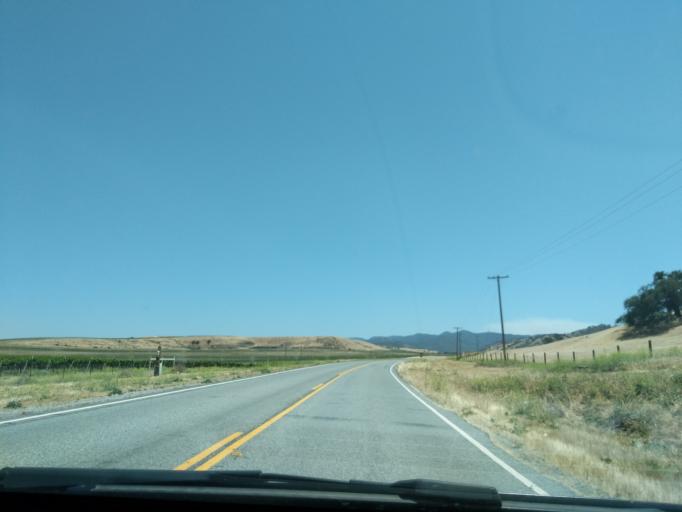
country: US
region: California
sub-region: Monterey County
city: King City
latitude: 36.1710
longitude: -121.1310
